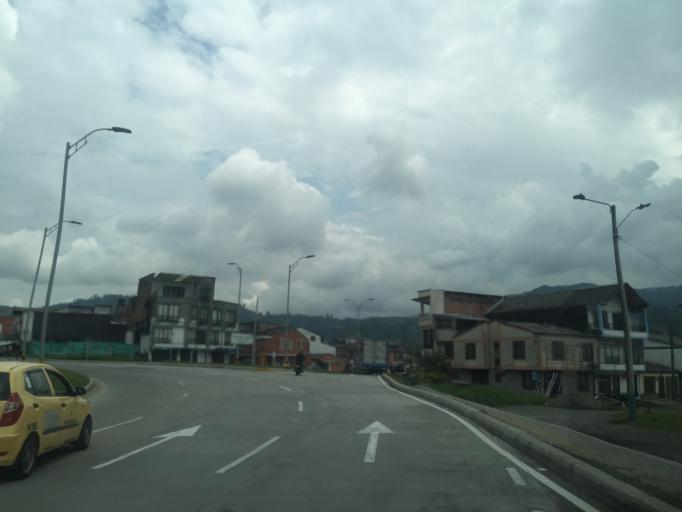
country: CO
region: Risaralda
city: Dos Quebradas
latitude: 4.8447
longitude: -75.6708
